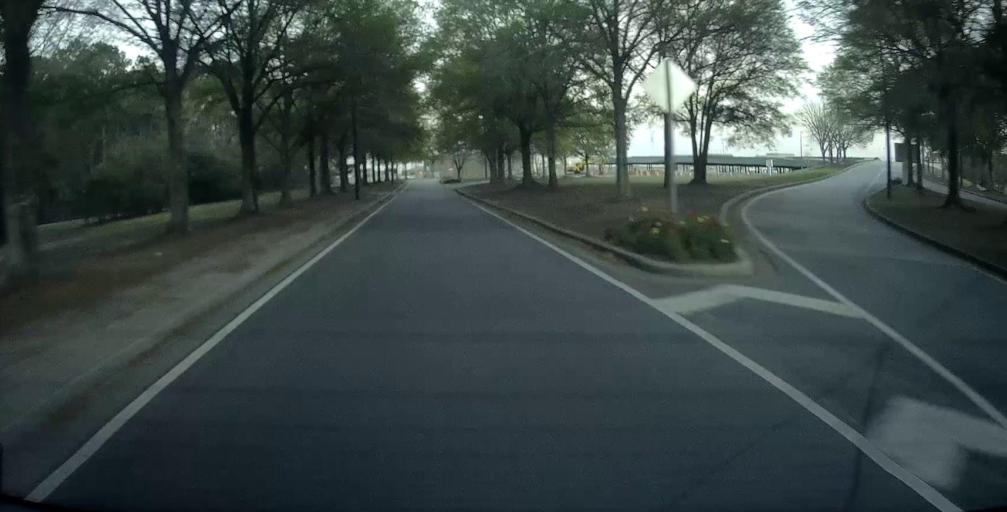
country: US
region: Georgia
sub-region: Chatham County
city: Pooler
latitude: 32.1382
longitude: -81.2118
